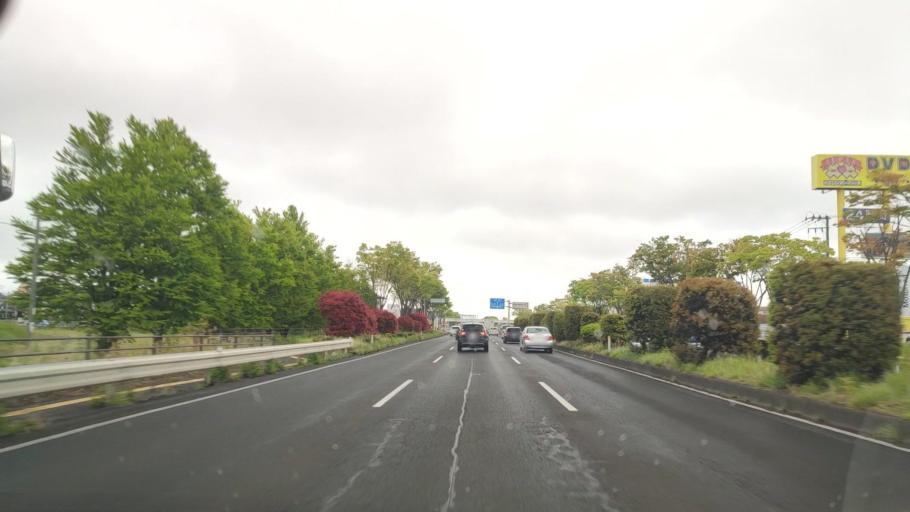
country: JP
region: Miyagi
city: Sendai
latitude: 38.2372
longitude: 140.9144
